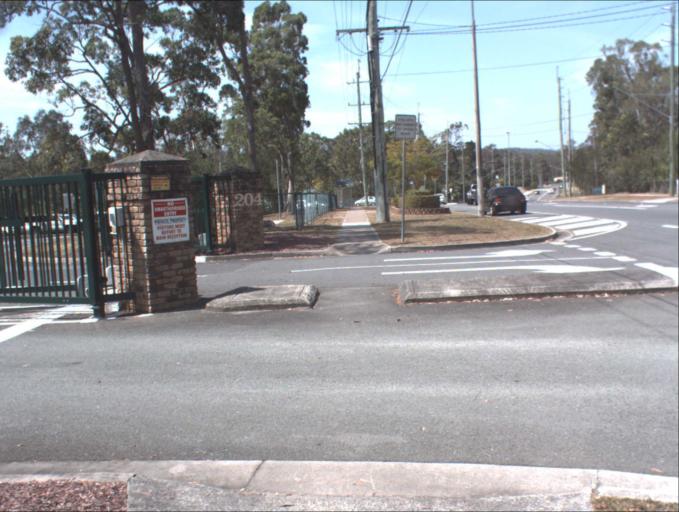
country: AU
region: Queensland
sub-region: Logan
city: Beenleigh
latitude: -27.6673
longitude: 153.2047
